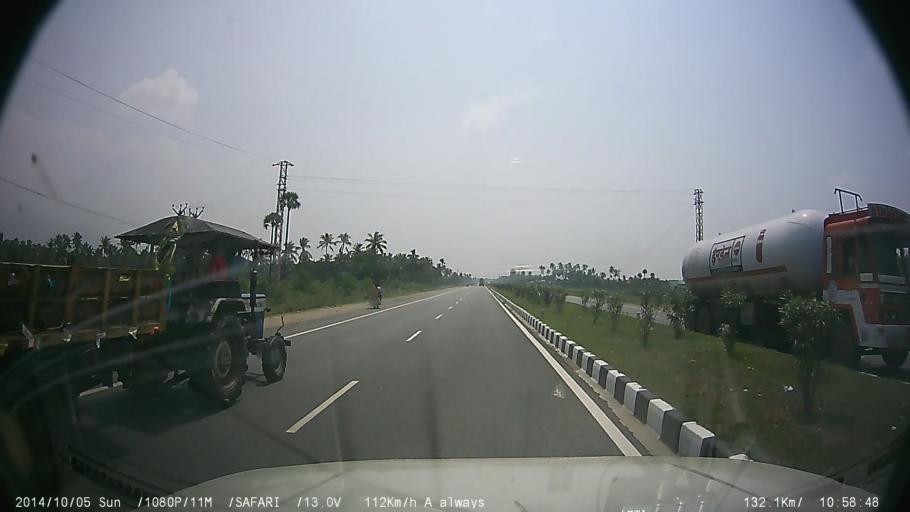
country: IN
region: Tamil Nadu
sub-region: Salem
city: Attur
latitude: 11.6404
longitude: 78.5214
